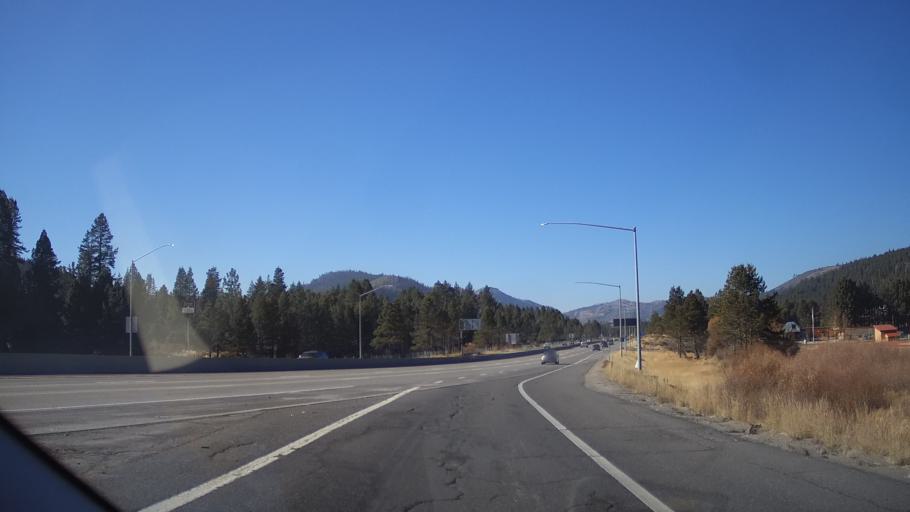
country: US
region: California
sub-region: Nevada County
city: Truckee
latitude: 39.3239
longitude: -120.2100
